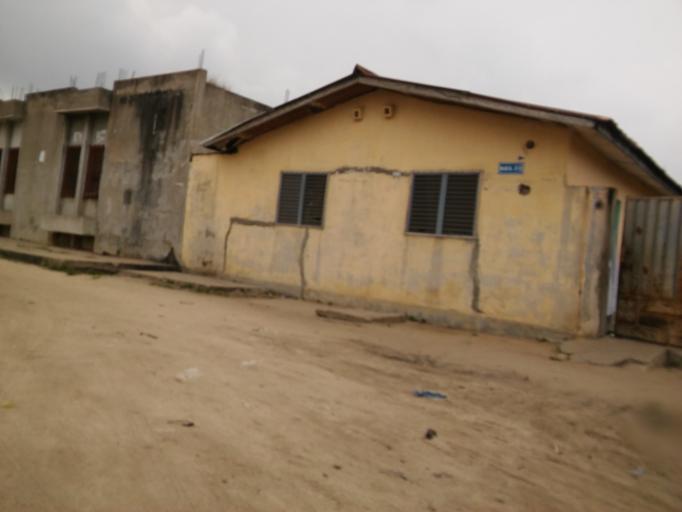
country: BJ
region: Littoral
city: Cotonou
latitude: 6.3924
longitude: 2.3720
